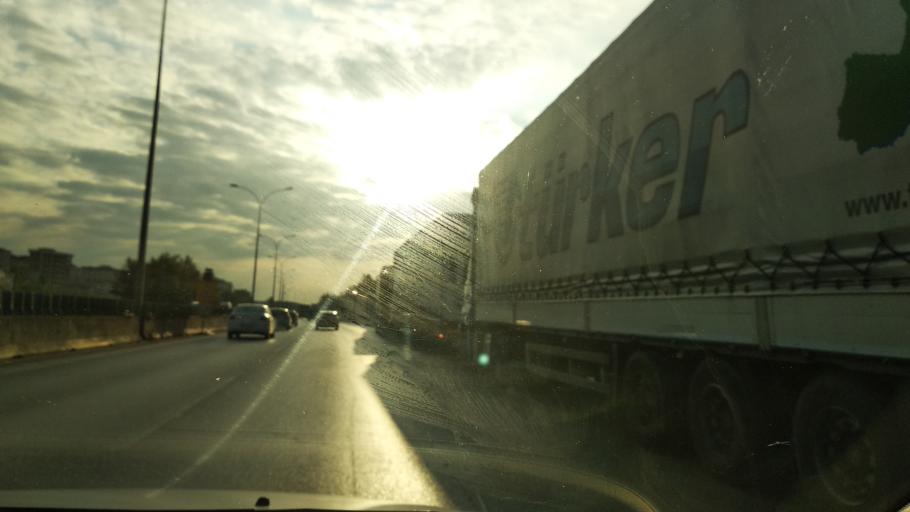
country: TR
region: Istanbul
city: Pendik
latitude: 40.8720
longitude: 29.2880
